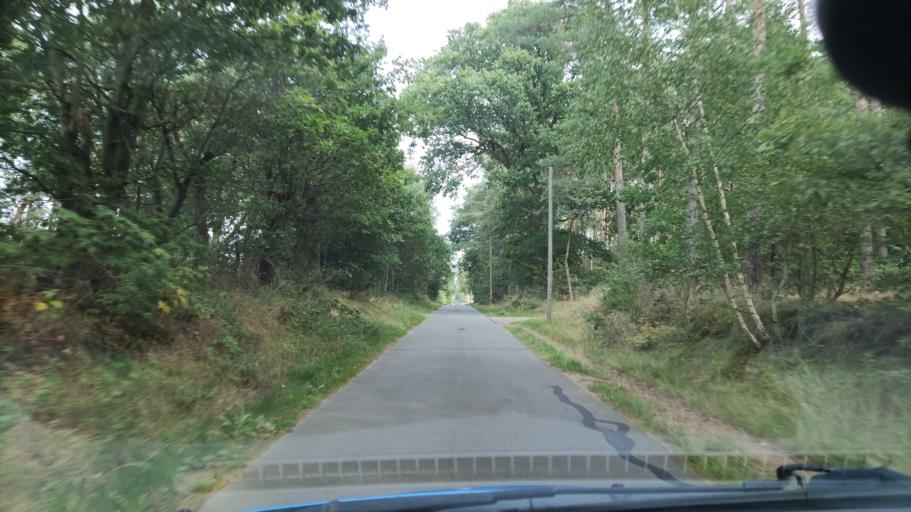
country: DE
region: Lower Saxony
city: Bienenbuttel
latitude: 53.1380
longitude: 10.5209
